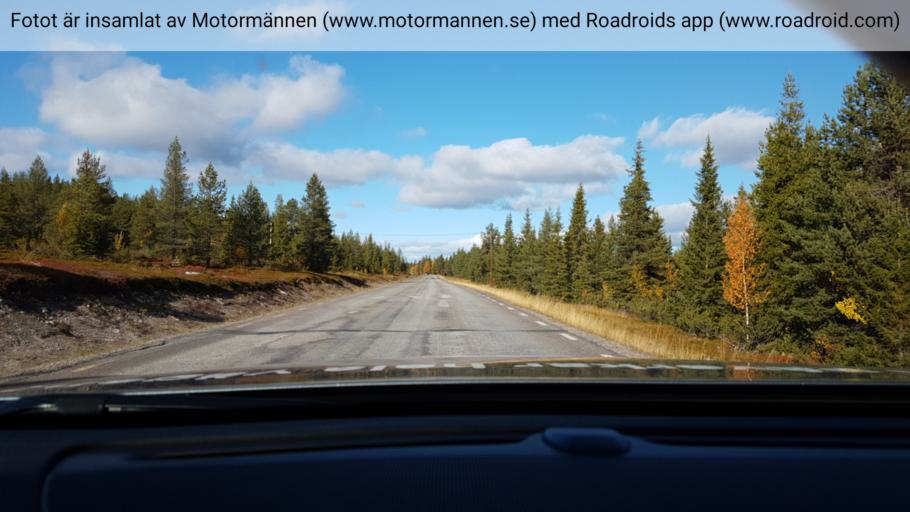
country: SE
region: Norrbotten
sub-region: Arjeplogs Kommun
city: Arjeplog
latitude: 65.9059
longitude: 18.3559
